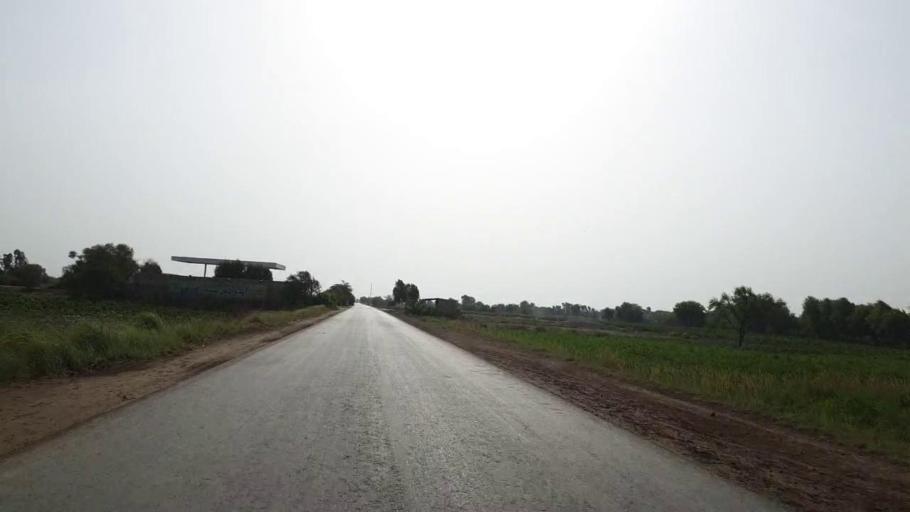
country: PK
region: Sindh
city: Nawabshah
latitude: 26.2649
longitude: 68.5051
